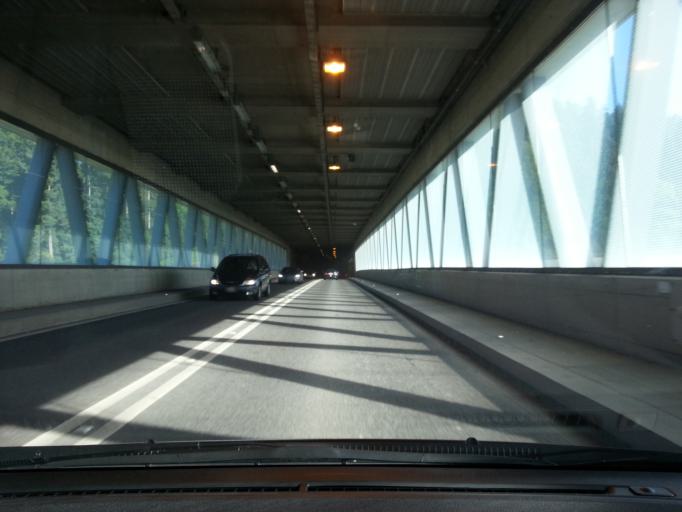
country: CH
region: Lucerne
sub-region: Lucerne-Land District
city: Buchrain
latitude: 47.0955
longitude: 8.3594
